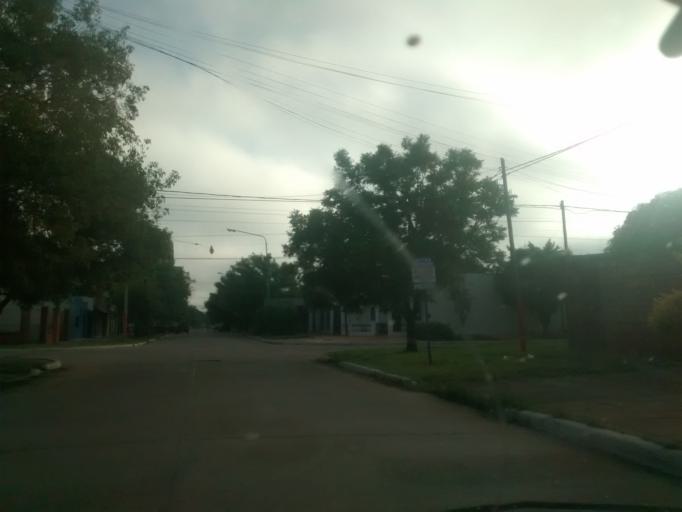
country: AR
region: Chaco
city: Resistencia
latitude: -27.4618
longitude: -58.9966
